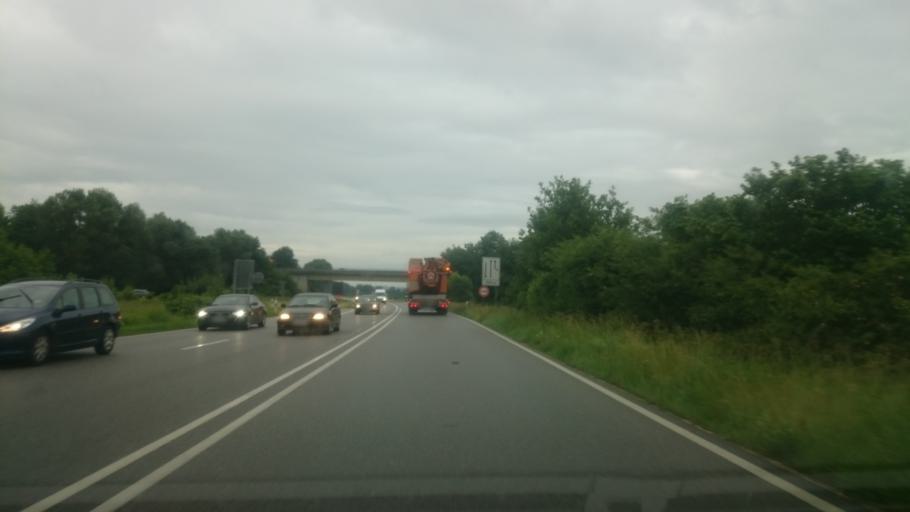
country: DE
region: Bavaria
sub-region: Upper Bavaria
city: Pornbach
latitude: 48.6261
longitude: 11.4437
